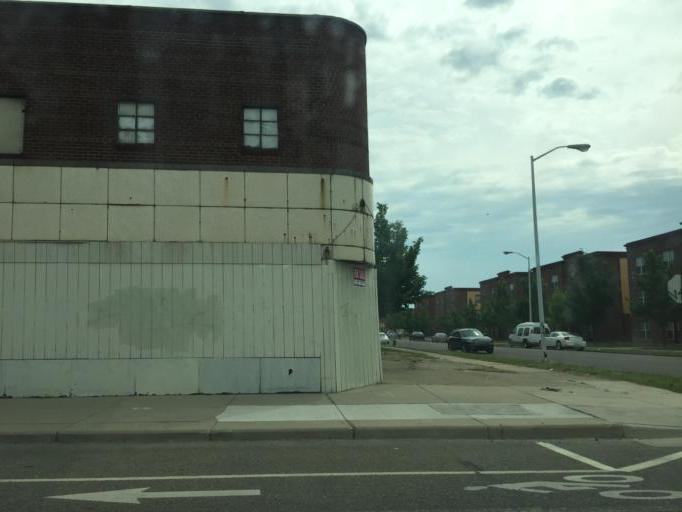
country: US
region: Michigan
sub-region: Wayne County
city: Detroit
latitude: 42.3457
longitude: -83.0660
